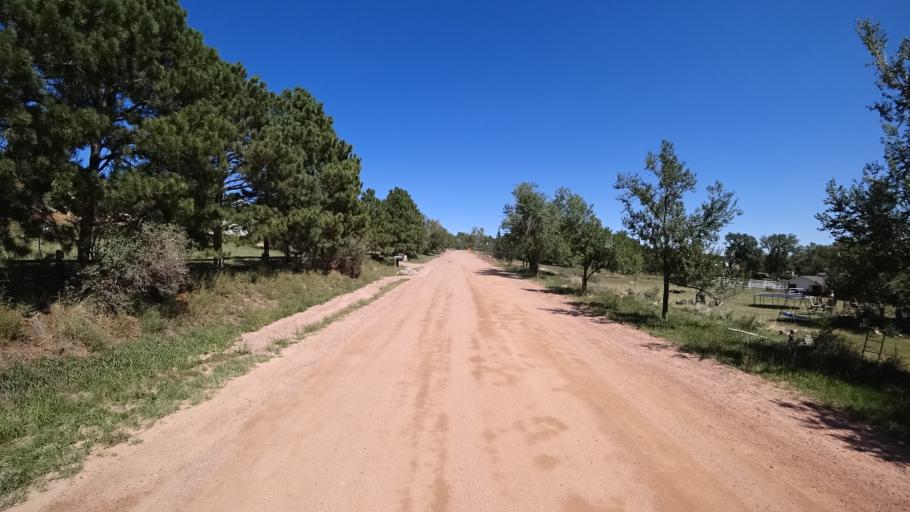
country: US
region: Colorado
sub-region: El Paso County
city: Cimarron Hills
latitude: 38.8648
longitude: -104.7384
